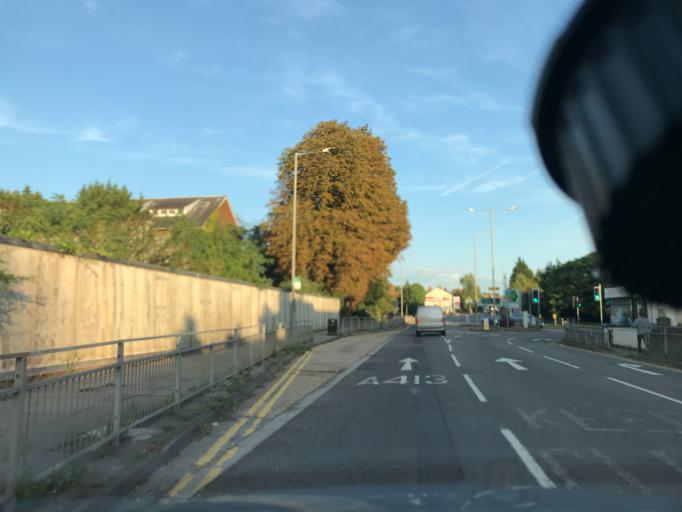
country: GB
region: England
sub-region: Buckinghamshire
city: Aylesbury
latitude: 51.8110
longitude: -0.8059
